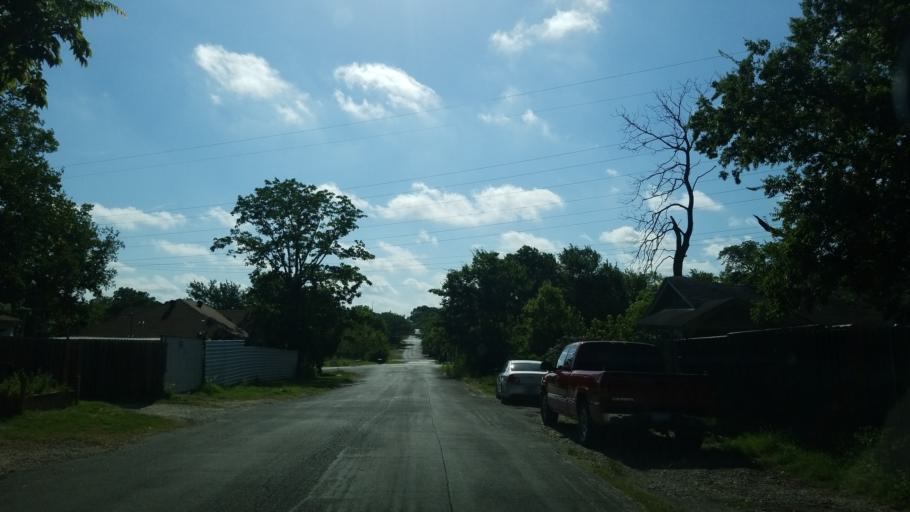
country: US
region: Texas
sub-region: Dallas County
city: Dallas
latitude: 32.7167
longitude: -96.8105
